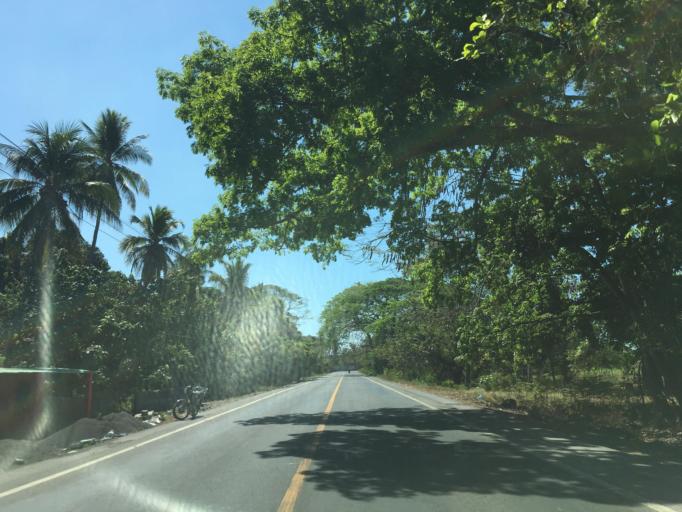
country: GT
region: Escuintla
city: Puerto San Jose
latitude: 13.9938
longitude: -90.8939
